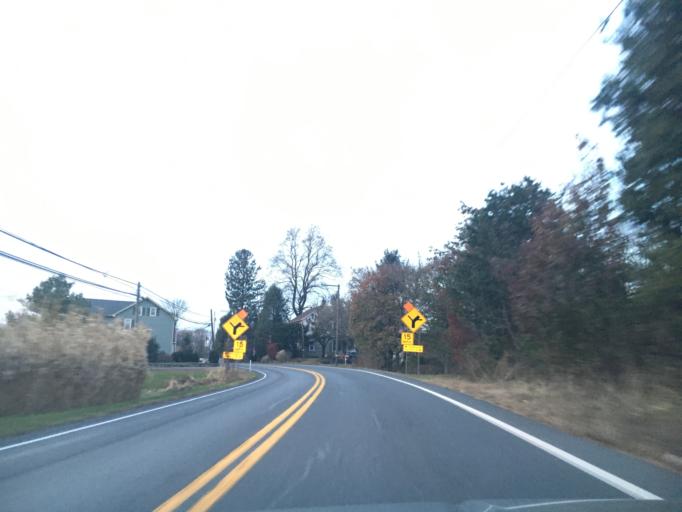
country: US
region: Pennsylvania
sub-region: Lehigh County
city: Egypt
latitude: 40.6493
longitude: -75.5354
